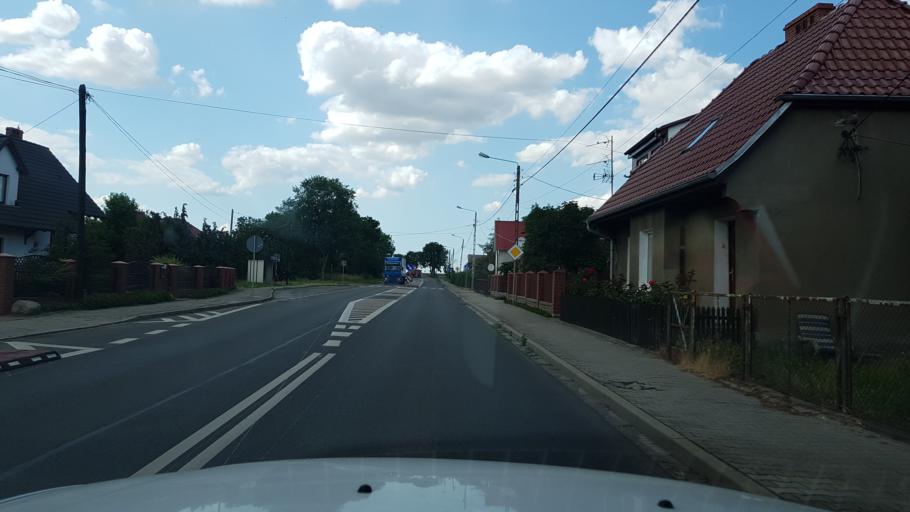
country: PL
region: West Pomeranian Voivodeship
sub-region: Powiat pyrzycki
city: Pyrzyce
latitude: 53.1874
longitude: 14.8391
